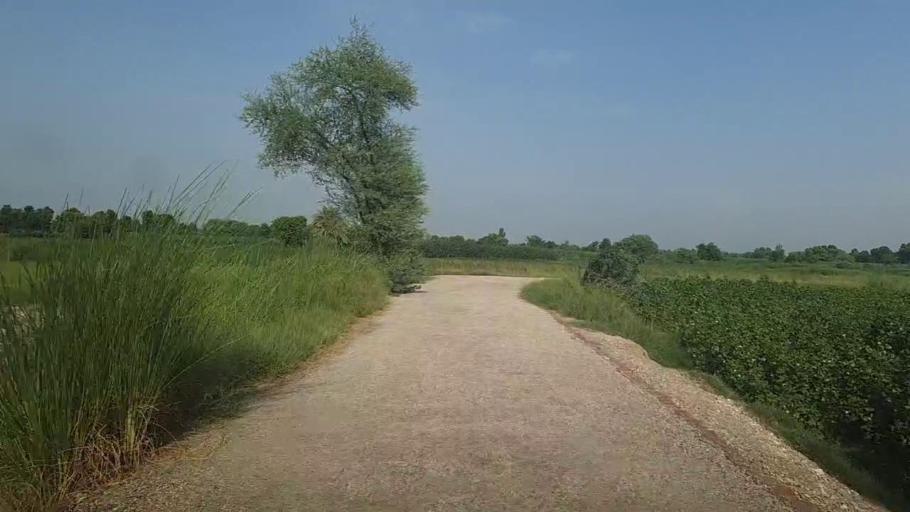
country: PK
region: Sindh
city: Ubauro
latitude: 28.1712
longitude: 69.7732
